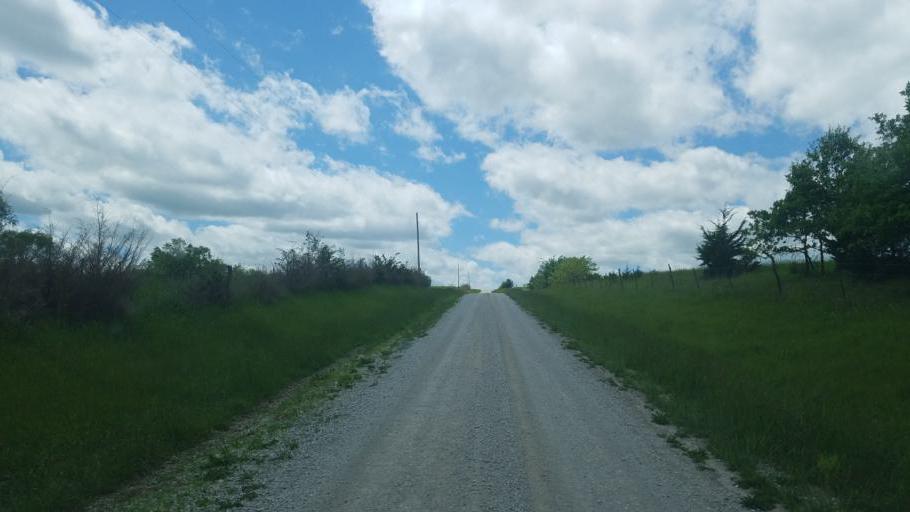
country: US
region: Iowa
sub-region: Decatur County
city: Lamoni
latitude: 40.5005
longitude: -94.0138
